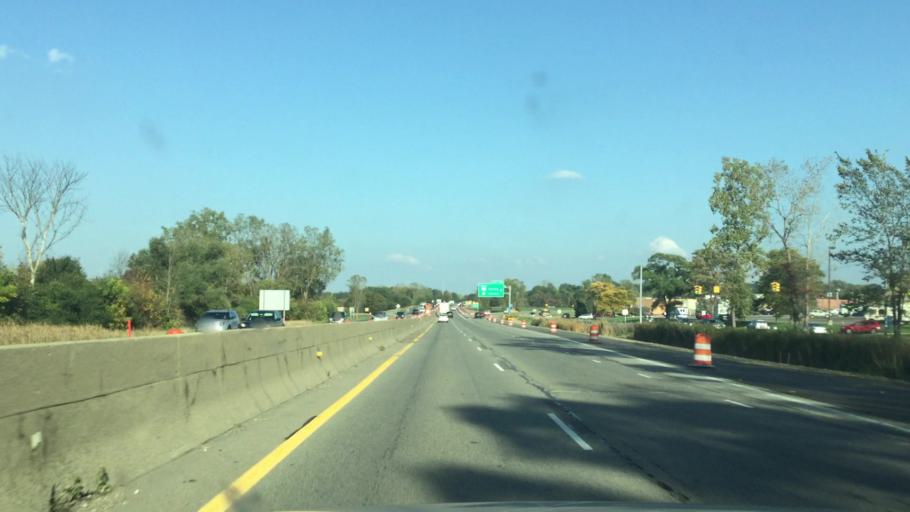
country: US
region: Michigan
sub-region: Jackson County
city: Jackson
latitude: 42.2702
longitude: -84.4344
